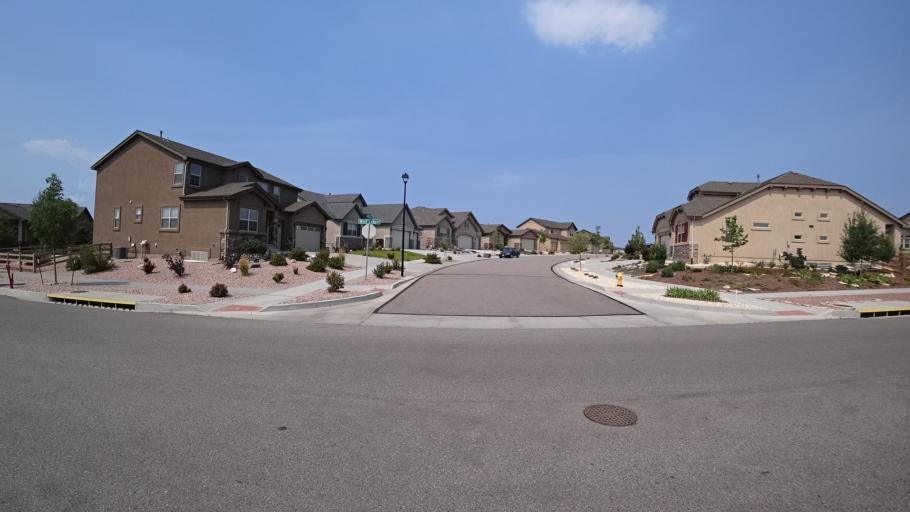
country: US
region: Colorado
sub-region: El Paso County
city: Black Forest
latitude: 38.9633
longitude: -104.7138
